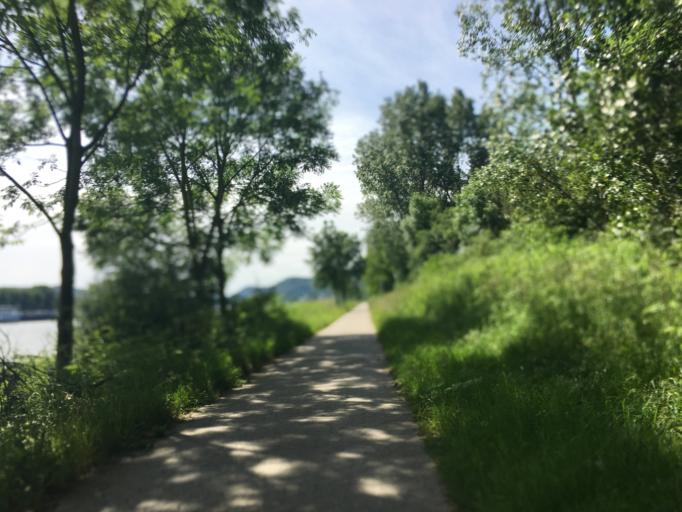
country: DE
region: Rheinland-Pfalz
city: Bad Breisig
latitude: 50.5252
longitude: 7.2914
